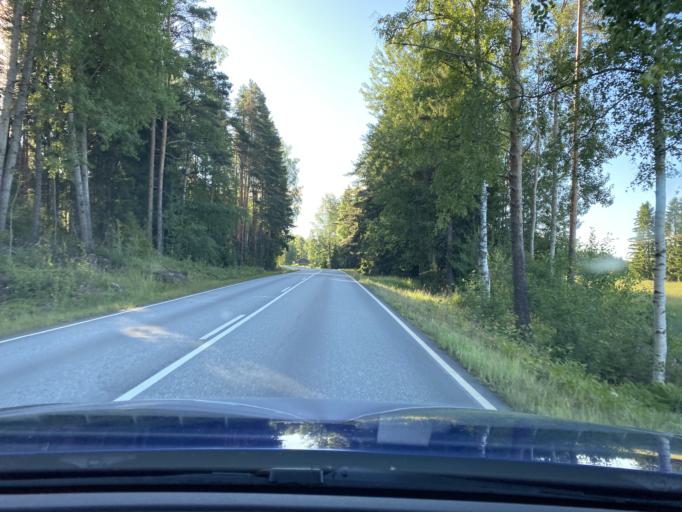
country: FI
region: Haeme
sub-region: Forssa
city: Humppila
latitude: 61.0938
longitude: 23.3696
